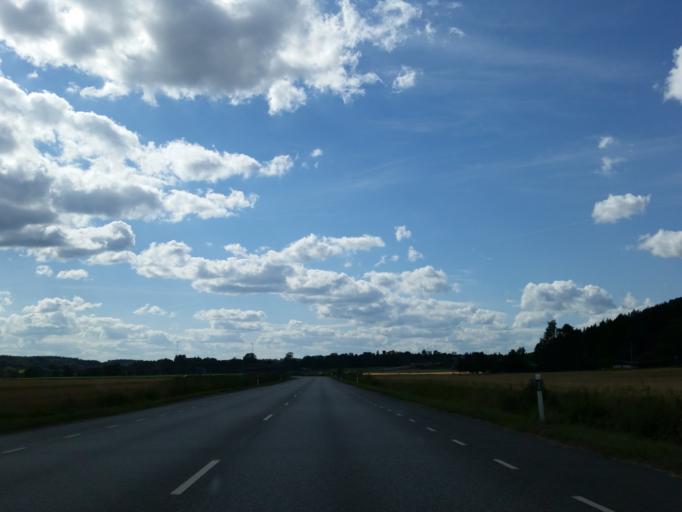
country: SE
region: Soedermanland
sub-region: Trosa Kommun
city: Vagnharad
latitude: 58.9464
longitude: 17.5248
